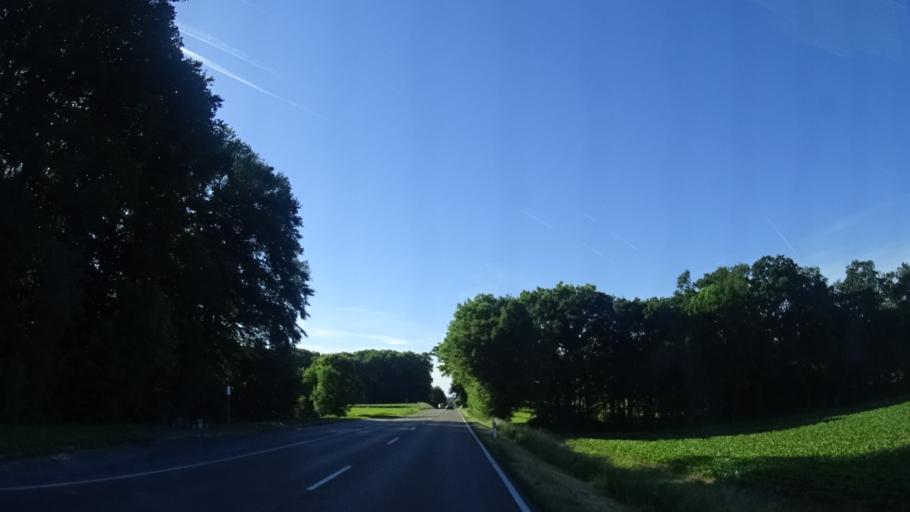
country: DE
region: Baden-Wuerttemberg
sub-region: Regierungsbezirk Stuttgart
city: Untermunkheim
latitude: 49.1838
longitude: 9.7026
